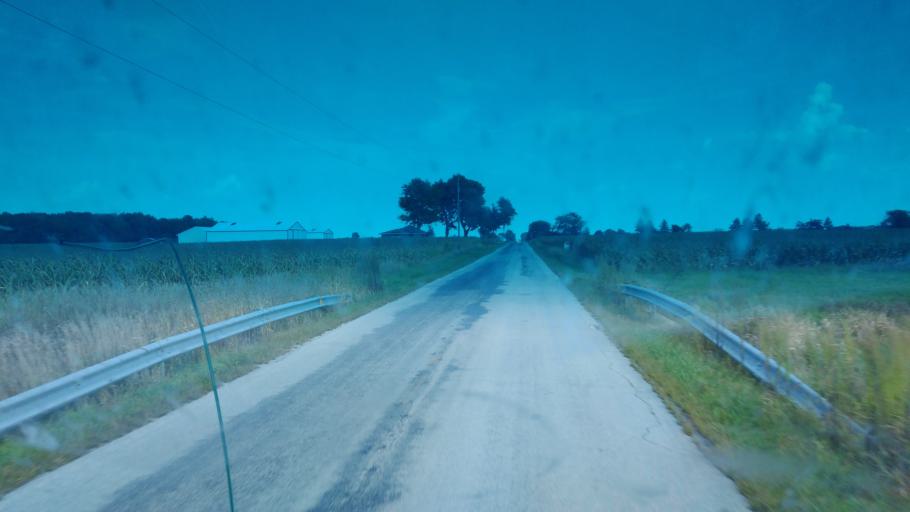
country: US
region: Ohio
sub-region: Hardin County
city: Forest
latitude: 40.9049
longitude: -83.4813
